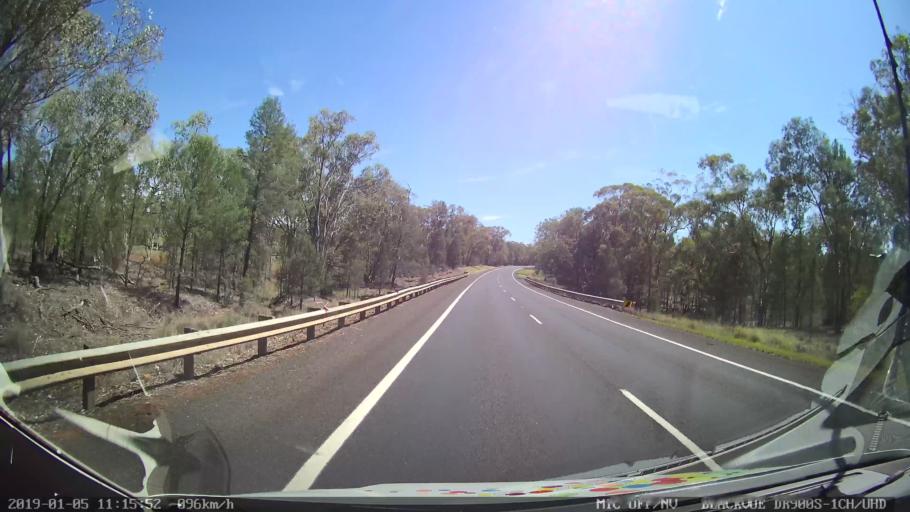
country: AU
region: New South Wales
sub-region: Warrumbungle Shire
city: Coonabarabran
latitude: -31.3468
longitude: 149.2963
